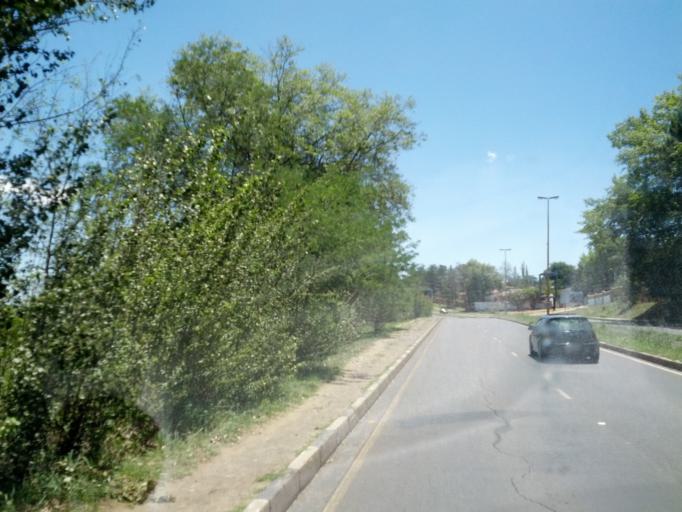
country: LS
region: Maseru
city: Maseru
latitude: -29.3093
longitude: 27.4740
